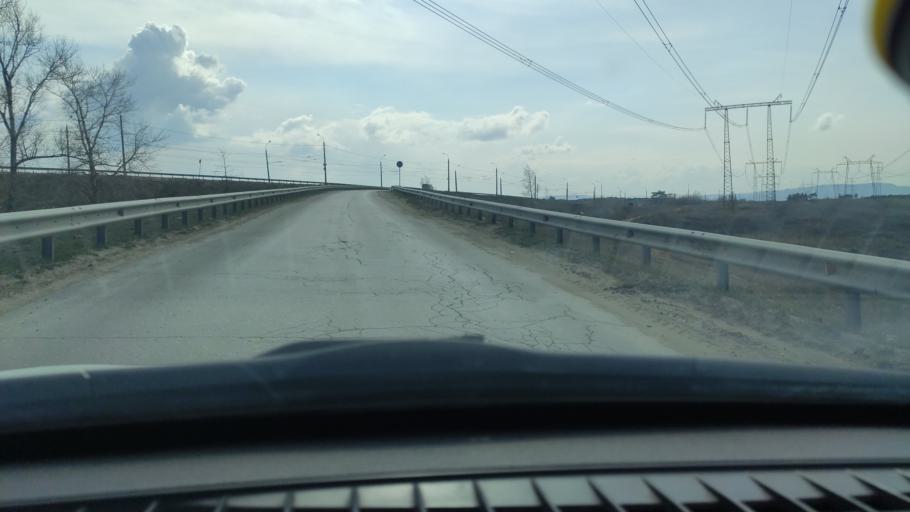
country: RU
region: Samara
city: Zhigulevsk
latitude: 53.5175
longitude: 49.5324
